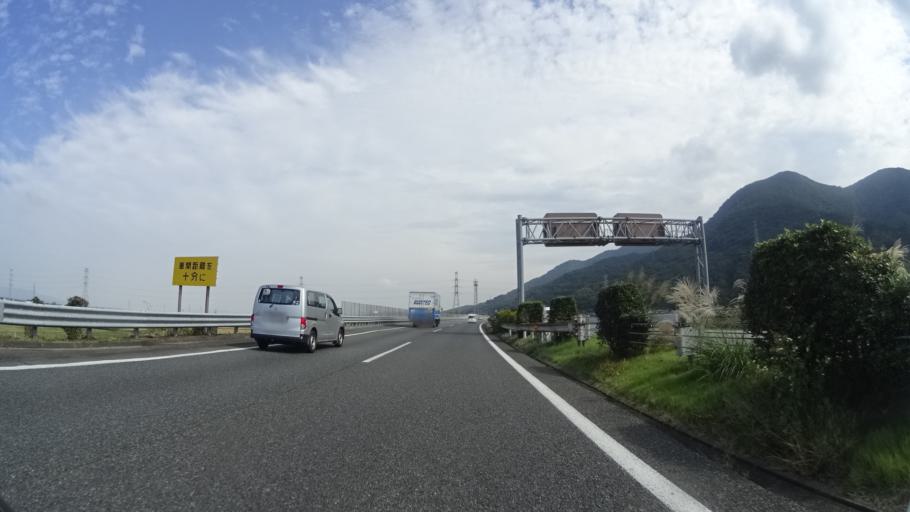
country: JP
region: Kumamoto
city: Yatsushiro
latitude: 32.5191
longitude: 130.6524
